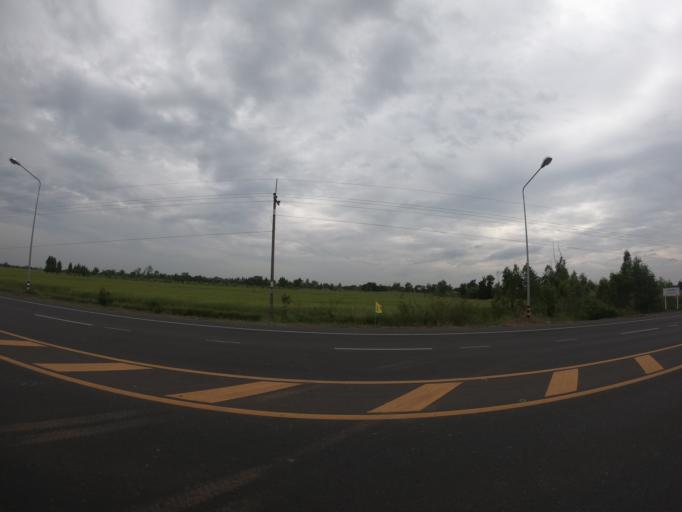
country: TH
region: Roi Et
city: Thawat Buri
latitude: 16.0901
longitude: 103.7682
